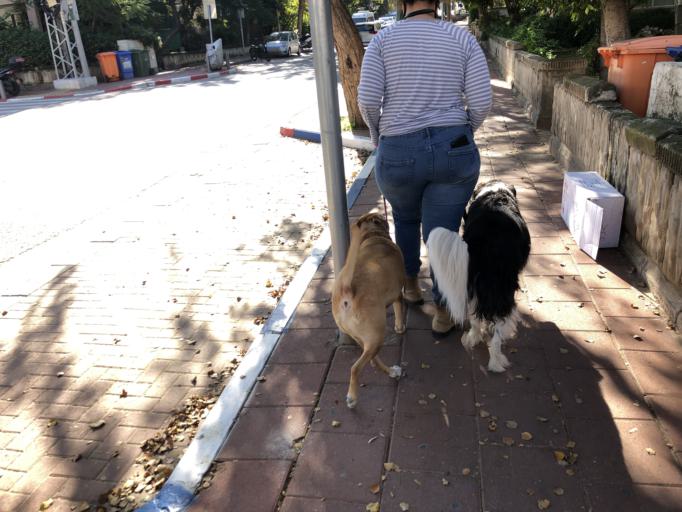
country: IL
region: Tel Aviv
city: Bene Beraq
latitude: 32.0765
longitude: 34.8251
